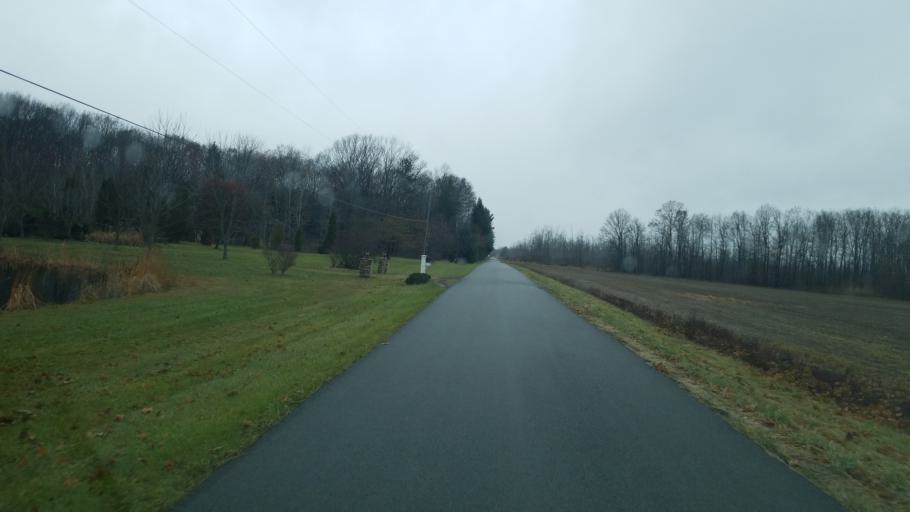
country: US
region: Ohio
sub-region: Ashtabula County
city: Andover
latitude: 41.5620
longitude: -80.7066
